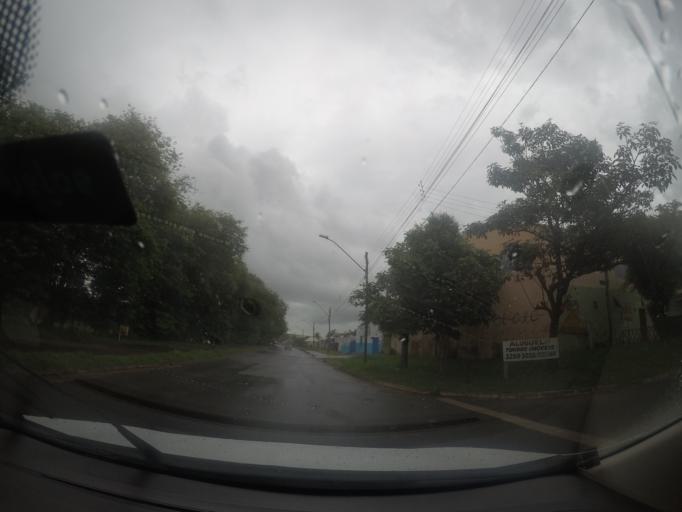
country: BR
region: Goias
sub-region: Trindade
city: Trindade
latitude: -16.6456
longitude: -49.3918
